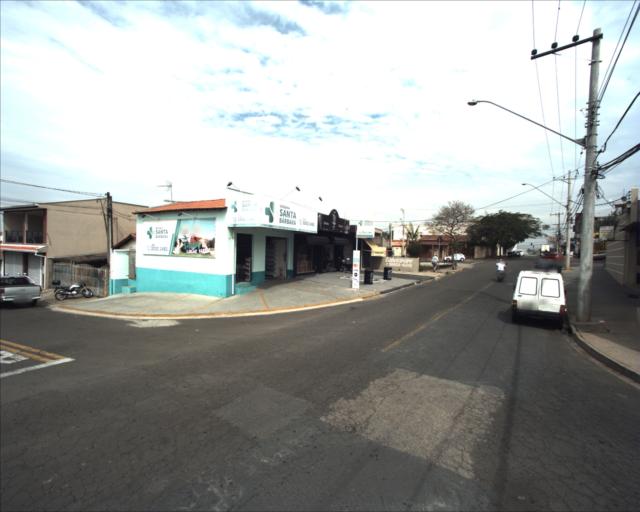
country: BR
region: Sao Paulo
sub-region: Sorocaba
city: Sorocaba
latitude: -23.5002
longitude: -47.5240
